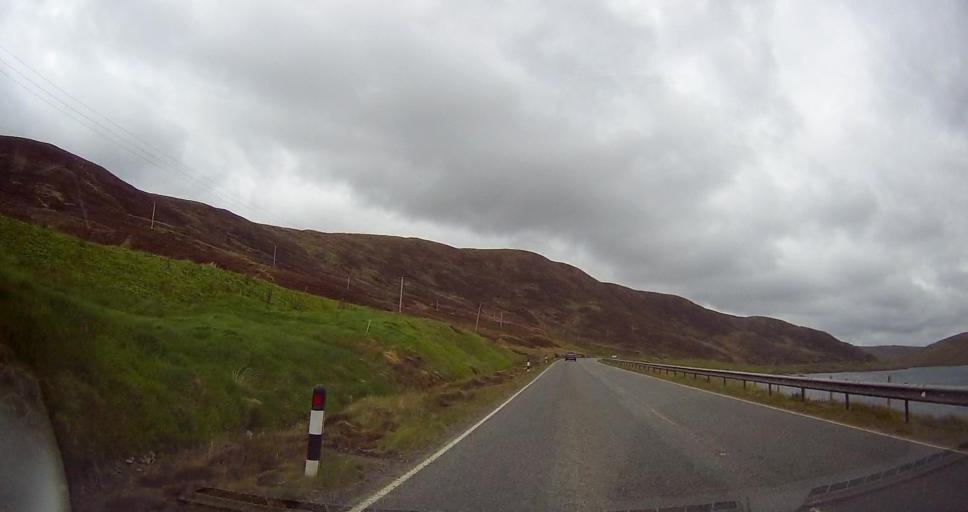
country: GB
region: Scotland
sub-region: Shetland Islands
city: Lerwick
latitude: 60.3695
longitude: -1.2994
